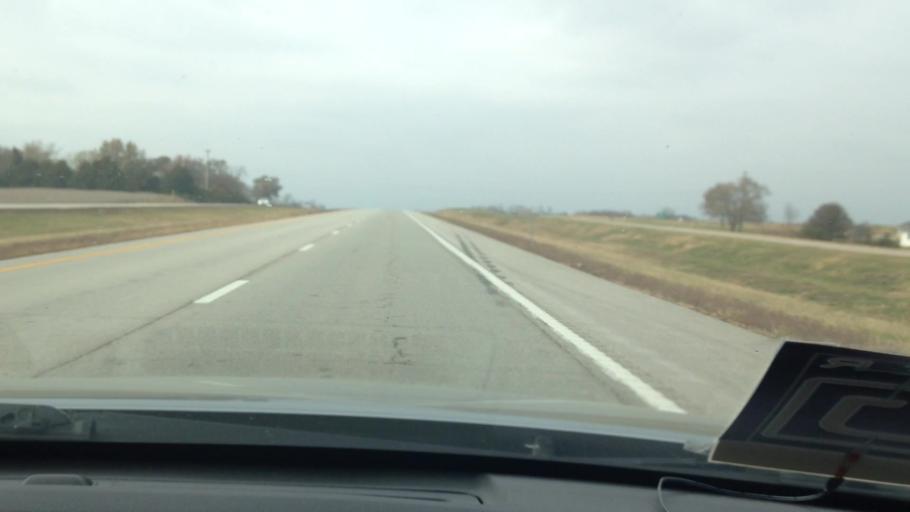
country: US
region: Missouri
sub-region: Cass County
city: Garden City
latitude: 38.5604
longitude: -94.1822
